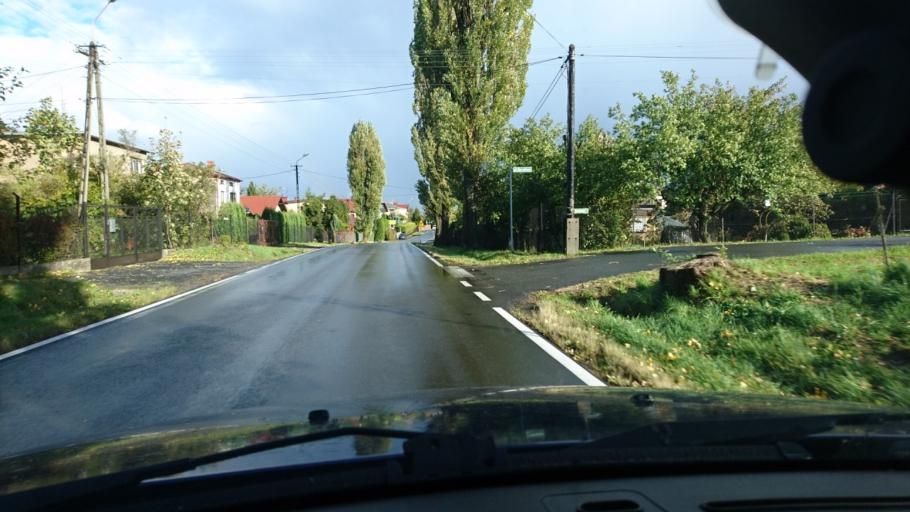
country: PL
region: Silesian Voivodeship
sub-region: Powiat bielski
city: Mazancowice
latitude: 49.8586
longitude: 19.0167
